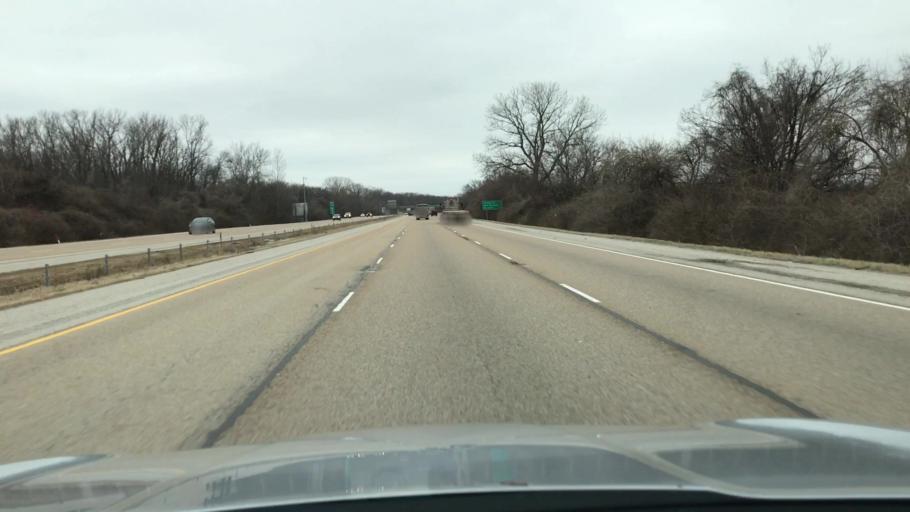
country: US
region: Illinois
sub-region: Saint Clair County
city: Fairmont City
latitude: 38.6649
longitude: -90.0587
